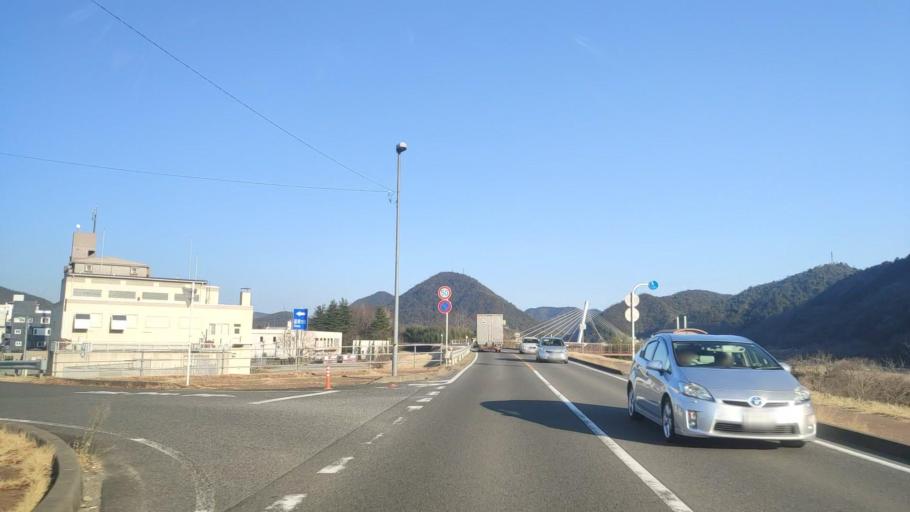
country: JP
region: Gifu
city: Gifu-shi
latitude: 35.4411
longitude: 136.7866
